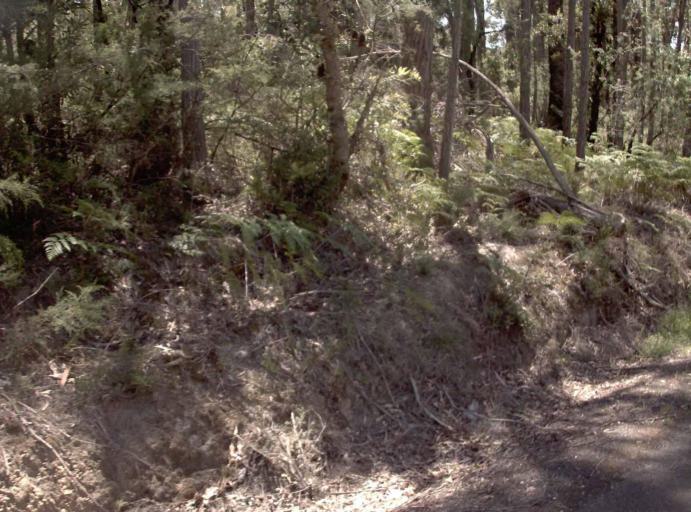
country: AU
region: Victoria
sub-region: East Gippsland
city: Lakes Entrance
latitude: -37.7402
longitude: 148.0786
